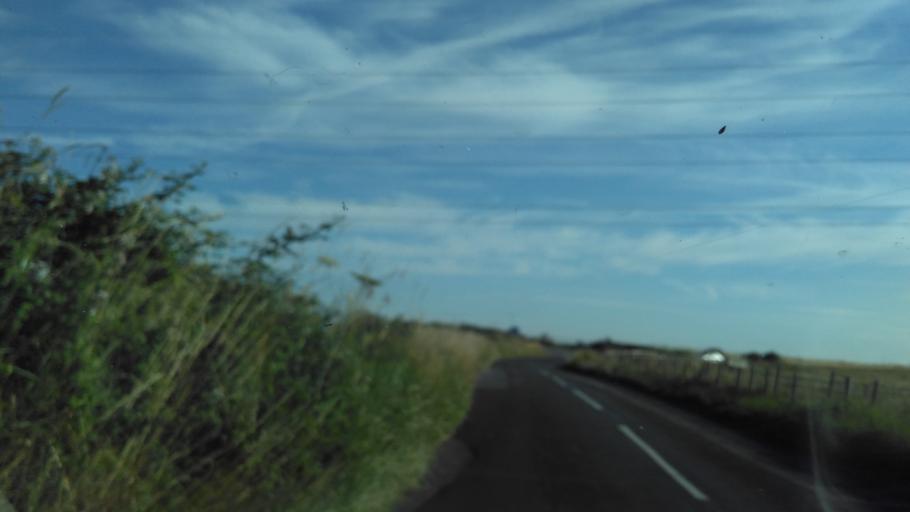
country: GB
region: England
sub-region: Kent
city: Dunkirk
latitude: 51.3363
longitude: 0.9520
